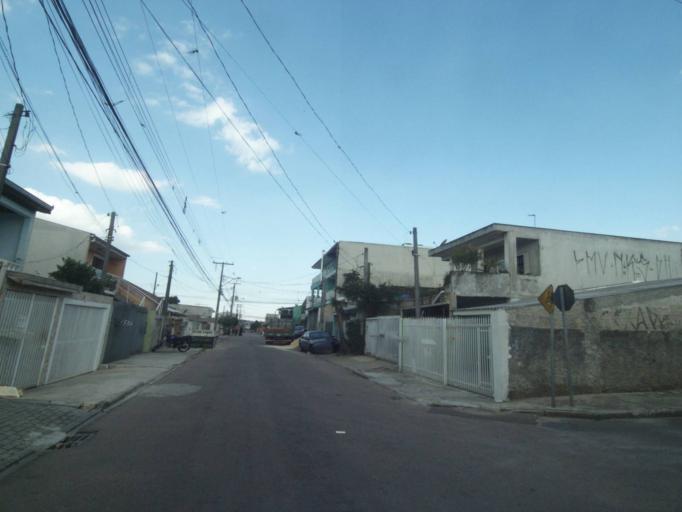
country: BR
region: Parana
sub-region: Sao Jose Dos Pinhais
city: Sao Jose dos Pinhais
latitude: -25.5324
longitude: -49.2768
